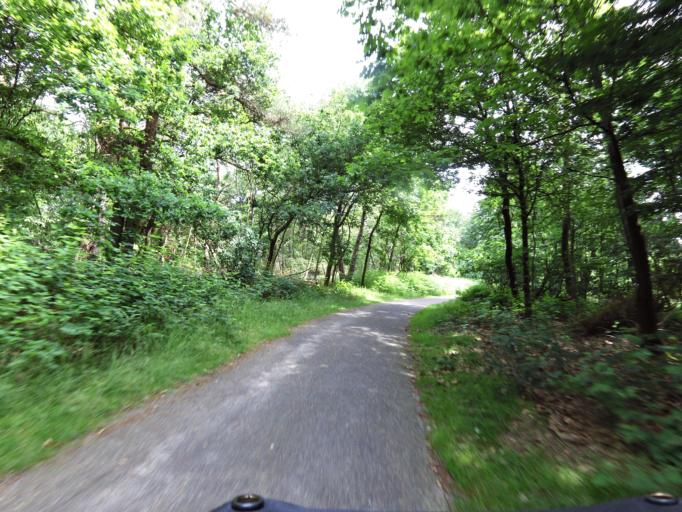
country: NL
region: Gelderland
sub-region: Gemeente Rozendaal
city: Rozendaal
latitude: 52.0225
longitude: 5.9805
